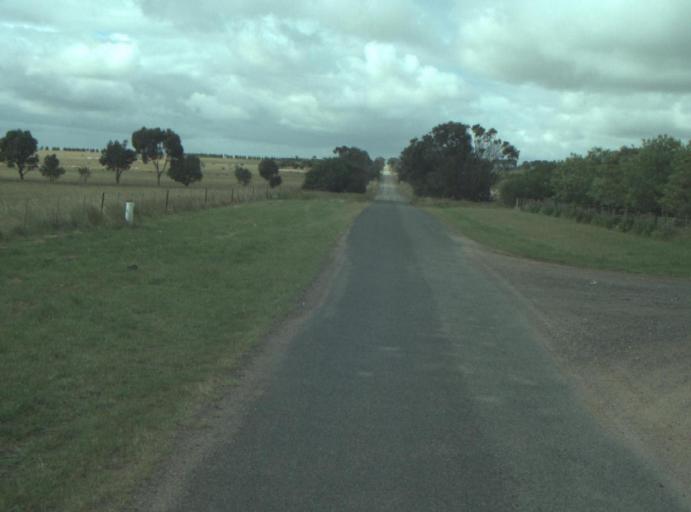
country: AU
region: Victoria
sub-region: Greater Geelong
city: Lara
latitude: -37.8632
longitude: 144.3247
